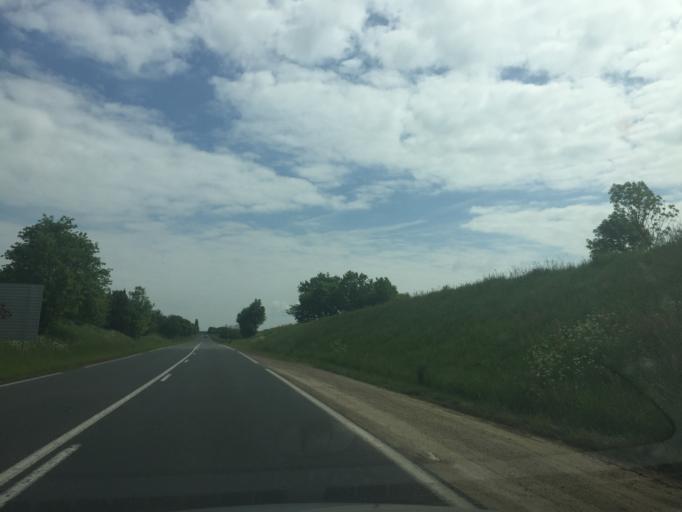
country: FR
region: Poitou-Charentes
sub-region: Departement de la Vienne
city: Lusignan
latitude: 46.4288
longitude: 0.1287
